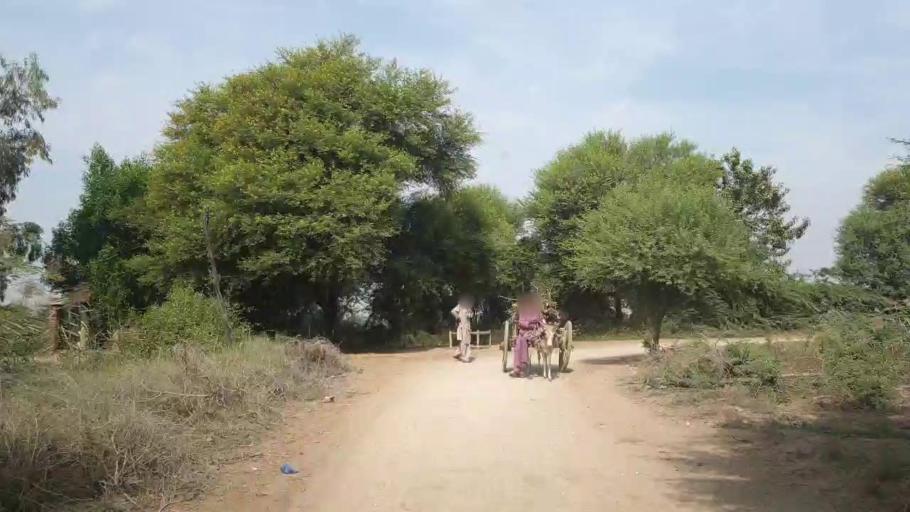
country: PK
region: Sindh
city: Rajo Khanani
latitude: 24.9671
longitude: 68.9948
